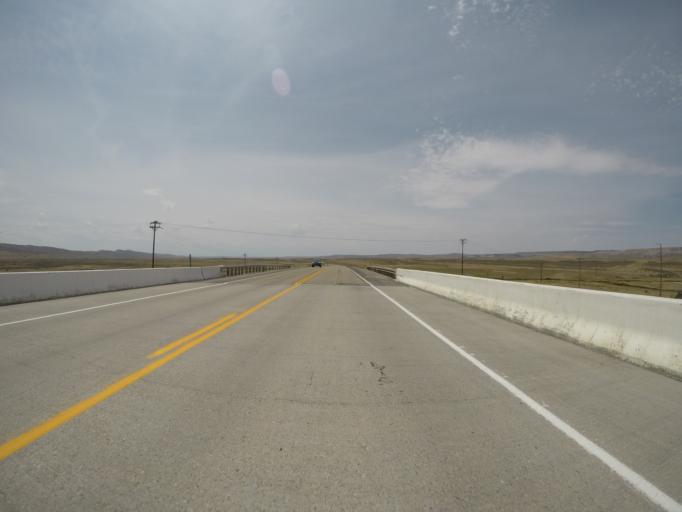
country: US
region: Wyoming
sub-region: Lincoln County
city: Kemmerer
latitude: 41.7311
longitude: -110.5670
